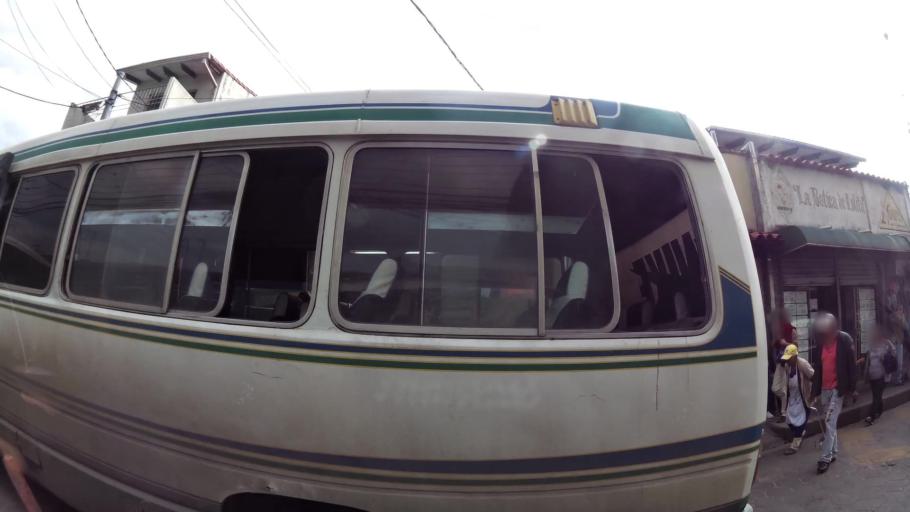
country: BO
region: Santa Cruz
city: Santa Cruz de la Sierra
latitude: -17.7788
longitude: -63.1792
